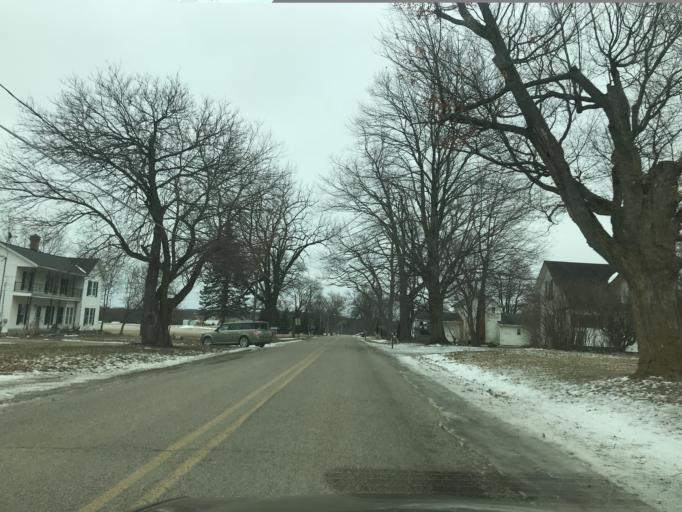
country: US
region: Michigan
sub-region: Jackson County
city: Brooklyn
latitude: 42.0679
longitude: -84.3260
